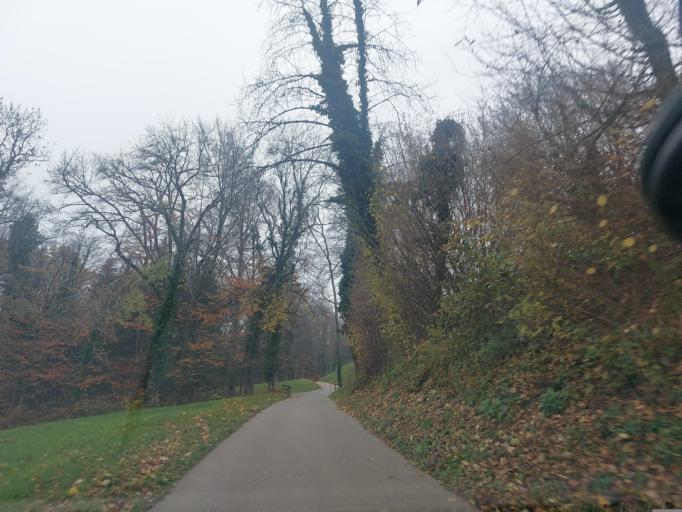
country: CH
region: Vaud
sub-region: Riviera-Pays-d'Enhaut District
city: Blonay
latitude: 46.4969
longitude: 6.8898
